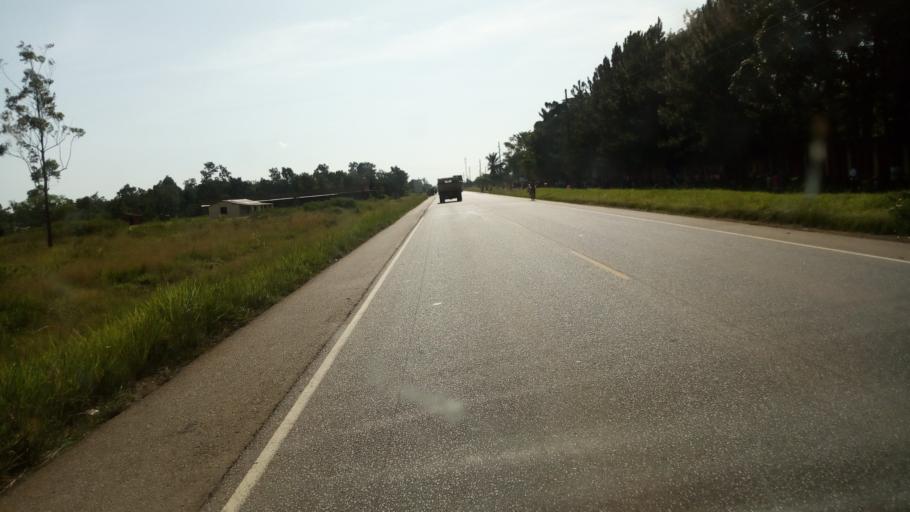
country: UG
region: Eastern Region
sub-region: Bugiri District
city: Bugiri
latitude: 0.5323
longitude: 33.8754
